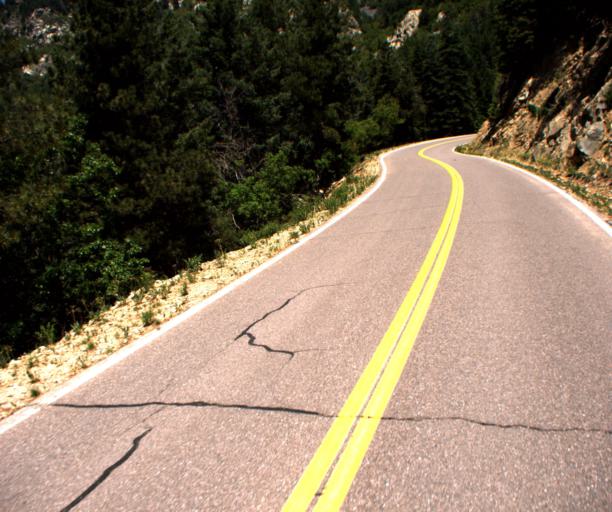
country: US
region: Arizona
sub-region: Graham County
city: Swift Trail Junction
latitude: 32.6394
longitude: -109.8489
